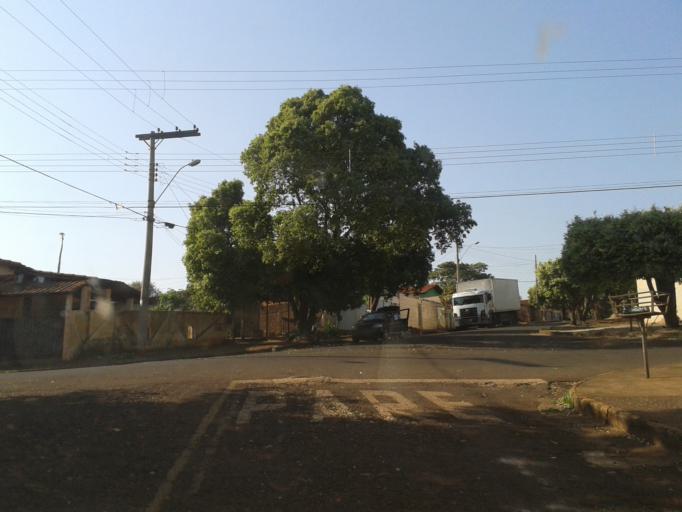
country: BR
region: Minas Gerais
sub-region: Ituiutaba
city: Ituiutaba
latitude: -18.9621
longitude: -49.4717
